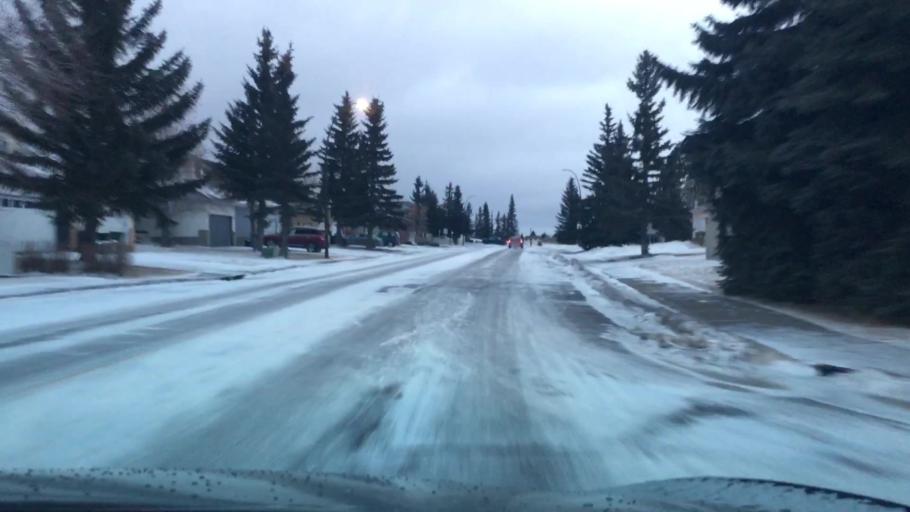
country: CA
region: Alberta
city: Calgary
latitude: 51.1341
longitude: -114.1673
